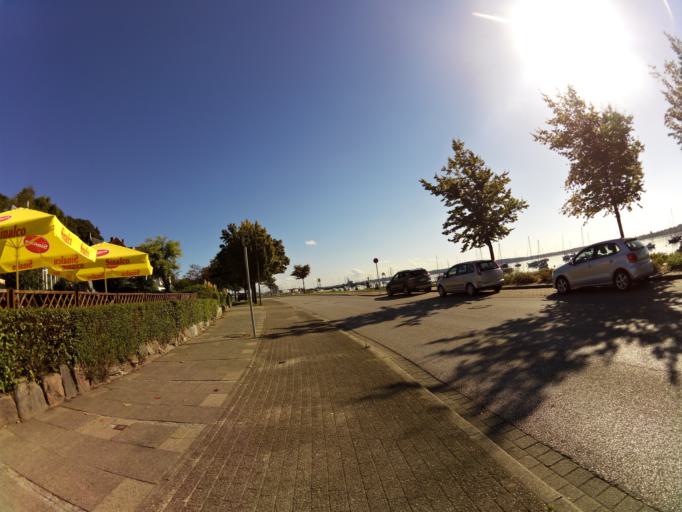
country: DE
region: Schleswig-Holstein
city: Eckernforde
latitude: 54.4771
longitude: 9.8447
